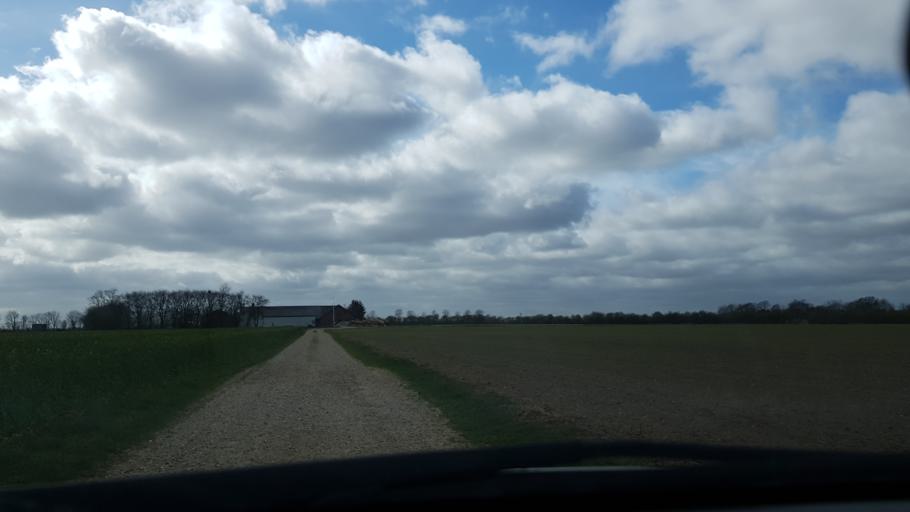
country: DK
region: South Denmark
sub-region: Vejen Kommune
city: Rodding
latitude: 55.3718
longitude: 8.9648
